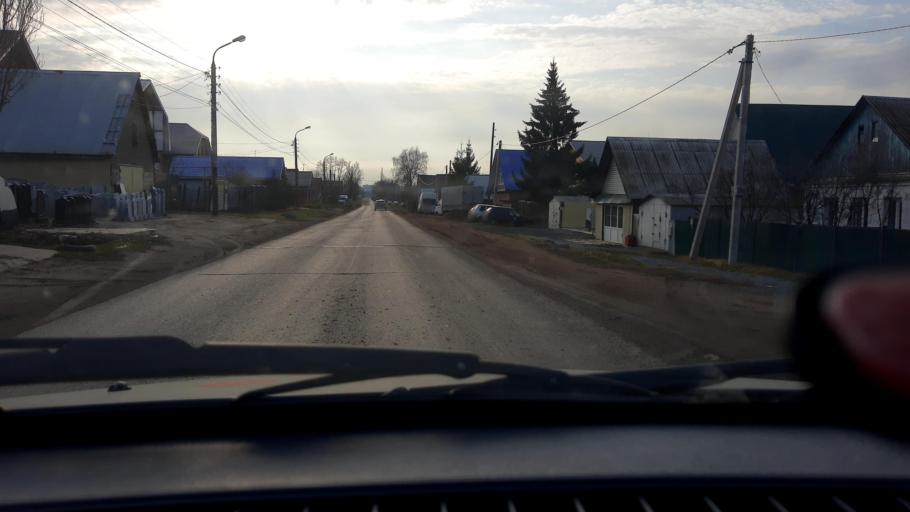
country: RU
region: Bashkortostan
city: Ufa
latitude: 54.8415
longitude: 56.1492
